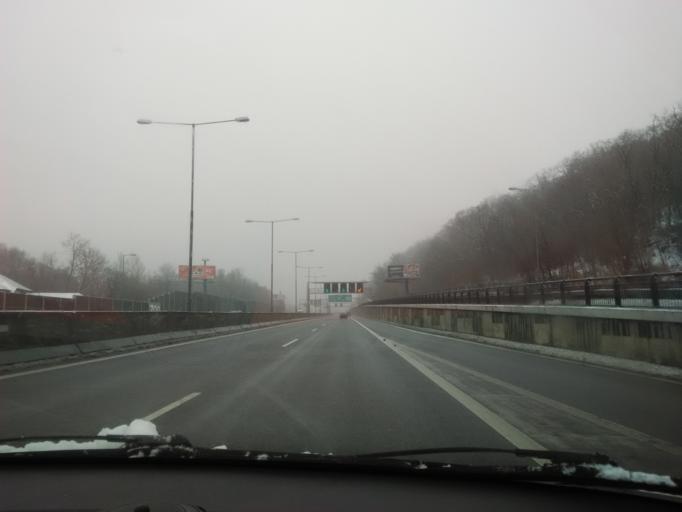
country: SK
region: Bratislavsky
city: Bratislava
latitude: 48.1557
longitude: 17.0766
